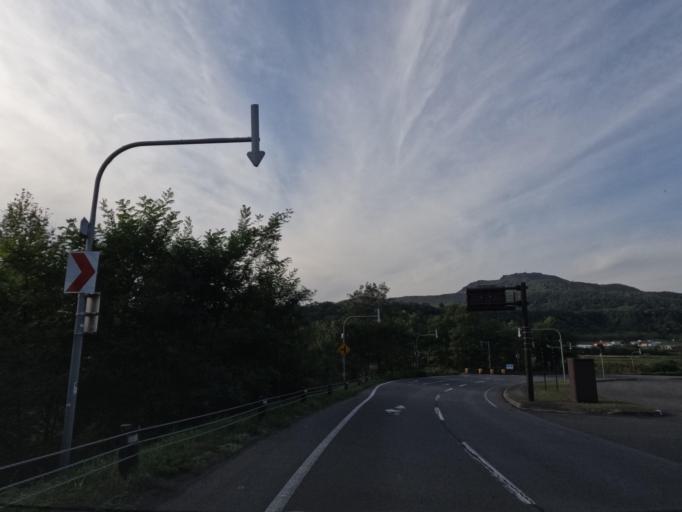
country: JP
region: Hokkaido
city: Date
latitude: 42.5084
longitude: 140.8619
